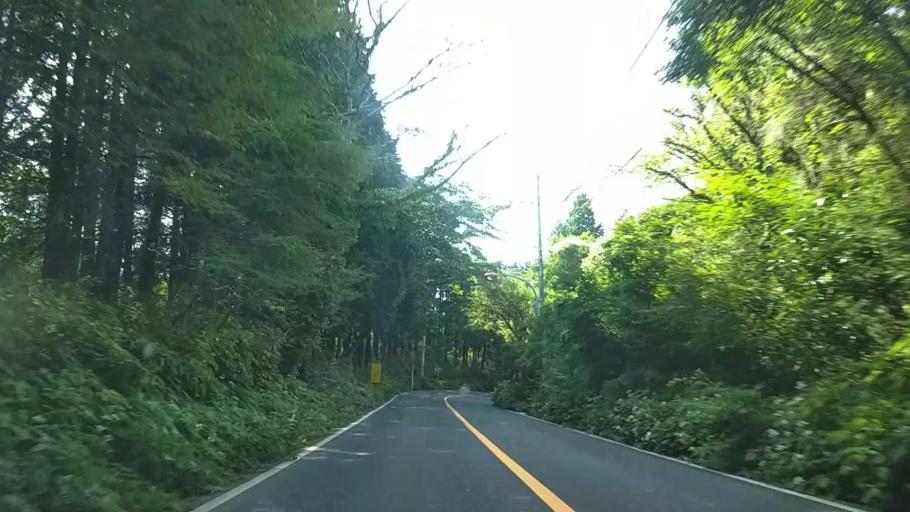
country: JP
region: Kanagawa
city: Hakone
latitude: 35.2075
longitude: 139.0226
